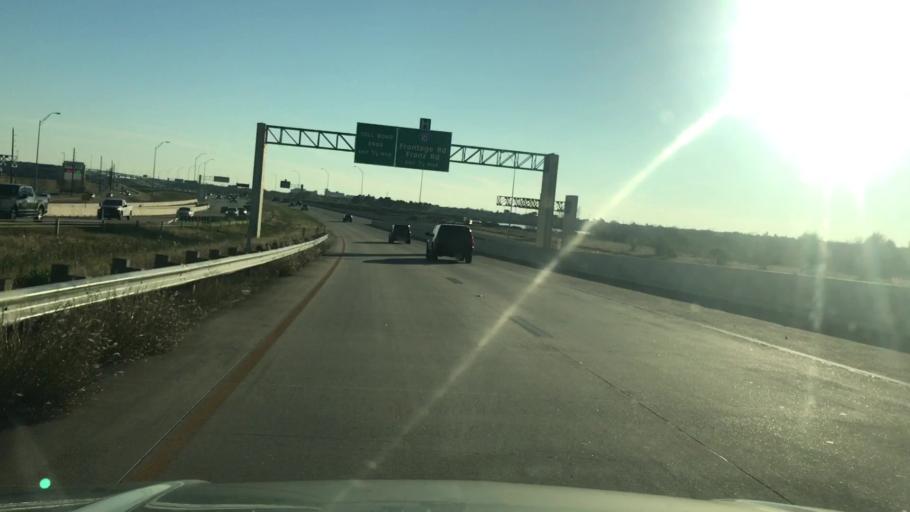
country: US
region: Texas
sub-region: Harris County
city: Katy
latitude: 29.8153
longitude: -95.7723
